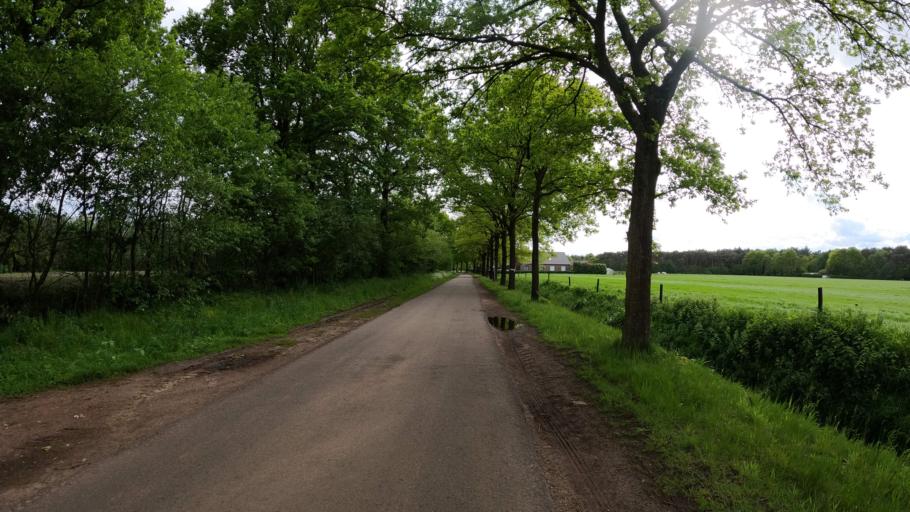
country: BE
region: Flanders
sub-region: Provincie Antwerpen
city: Lille
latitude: 51.2485
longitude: 4.8744
